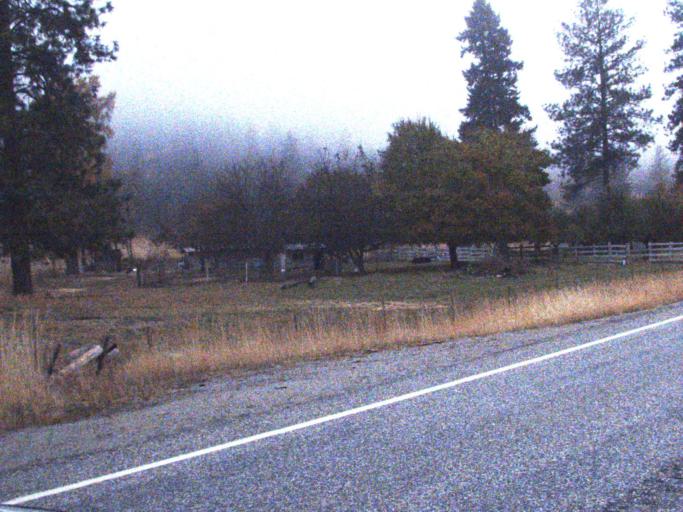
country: US
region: Washington
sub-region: Stevens County
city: Kettle Falls
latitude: 48.7133
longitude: -118.1325
